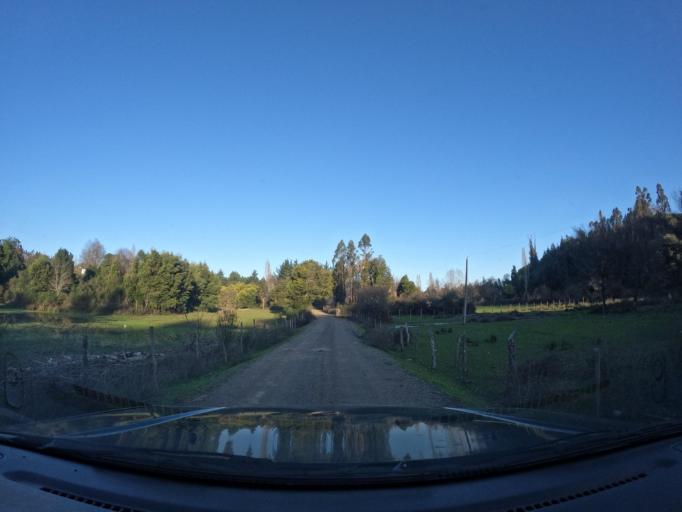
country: CL
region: Biobio
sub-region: Provincia de Concepcion
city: Chiguayante
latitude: -37.0174
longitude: -72.8353
